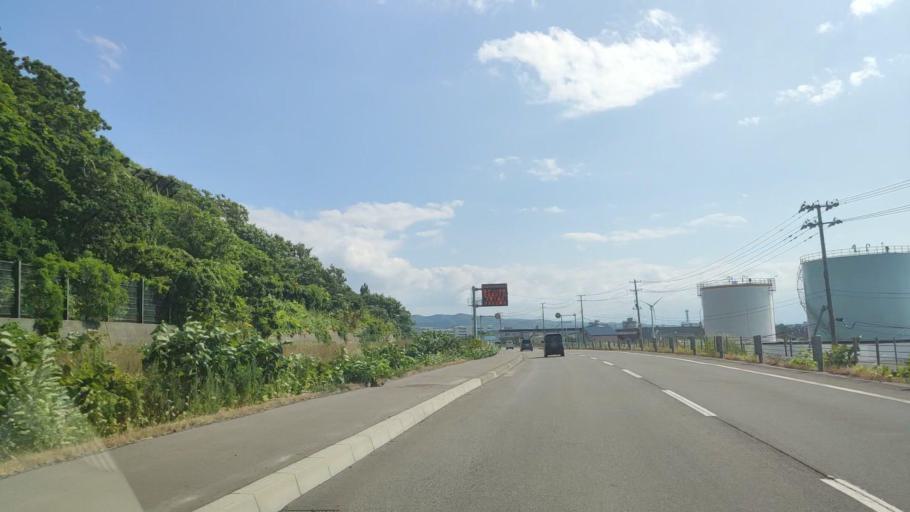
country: JP
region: Hokkaido
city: Rumoi
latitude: 43.9572
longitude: 141.6442
